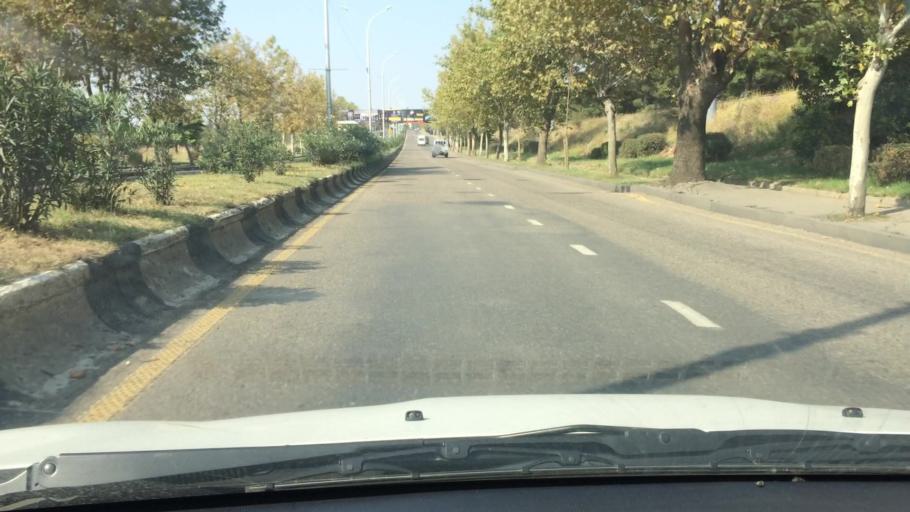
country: GE
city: Didi Lilo
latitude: 41.6803
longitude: 44.9577
